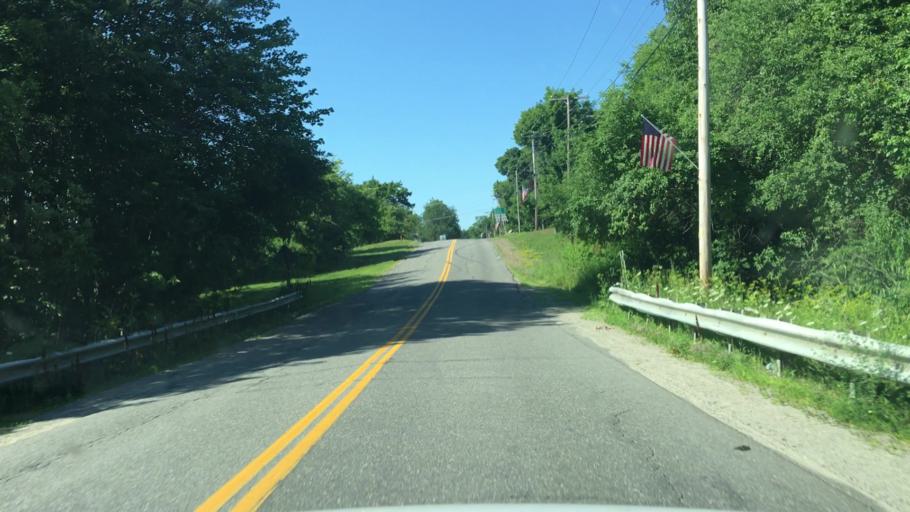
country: US
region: Maine
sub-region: Penobscot County
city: Enfield
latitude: 45.2473
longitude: -68.5659
